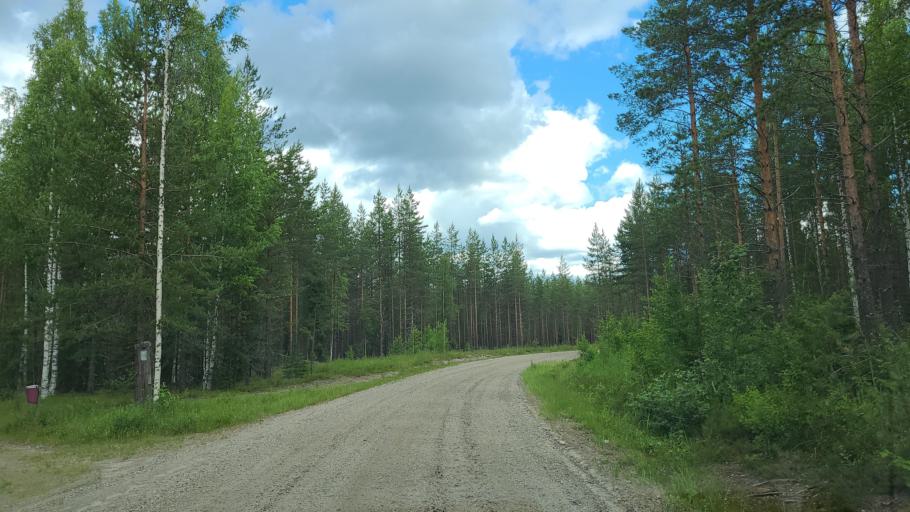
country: FI
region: Northern Savo
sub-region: Koillis-Savo
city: Kaavi
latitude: 63.0425
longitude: 28.8127
